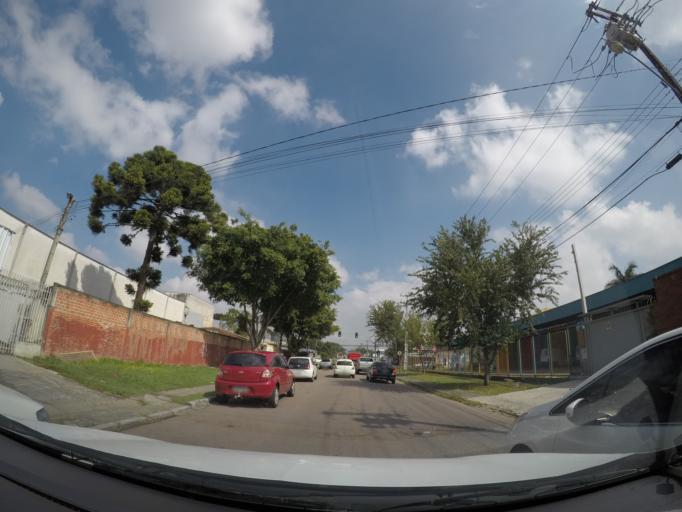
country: BR
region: Parana
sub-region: Sao Jose Dos Pinhais
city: Sao Jose dos Pinhais
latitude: -25.4987
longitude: -49.2369
